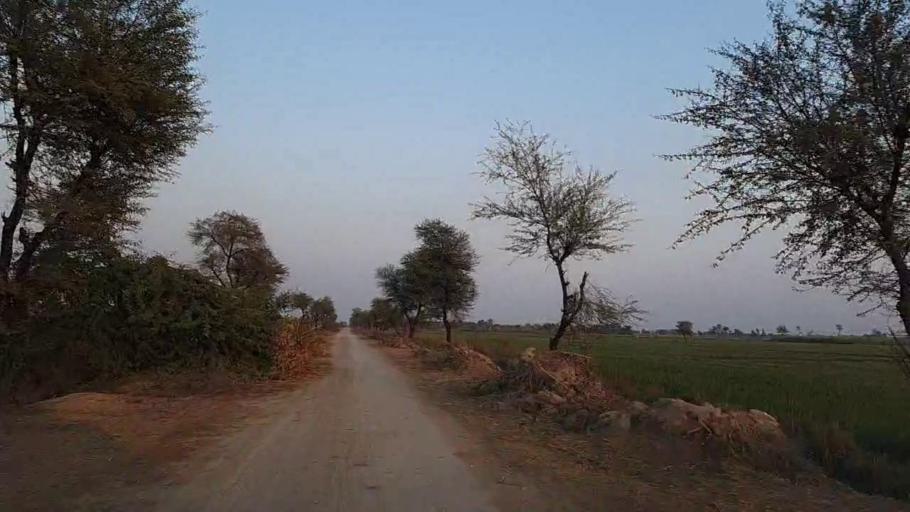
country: PK
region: Sindh
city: Jam Sahib
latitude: 26.3049
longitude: 68.5705
